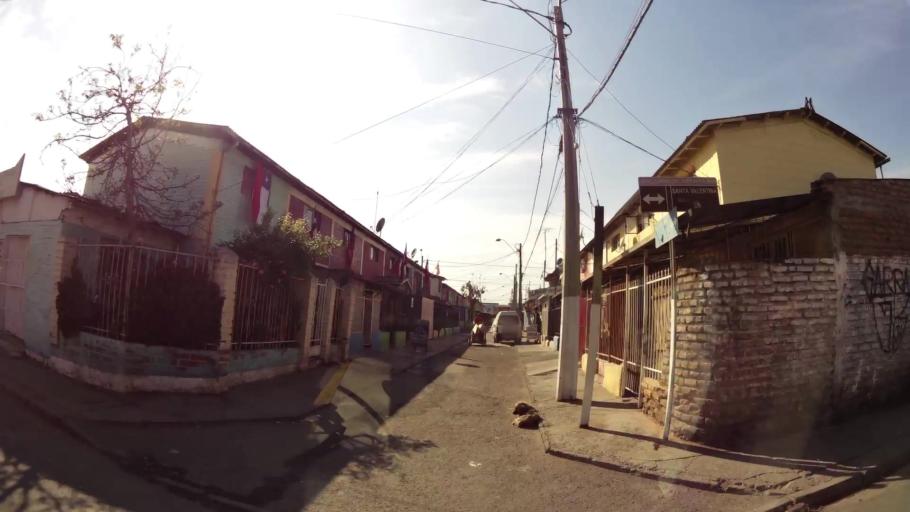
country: CL
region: Santiago Metropolitan
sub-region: Provincia de Santiago
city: La Pintana
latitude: -33.5642
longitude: -70.6368
